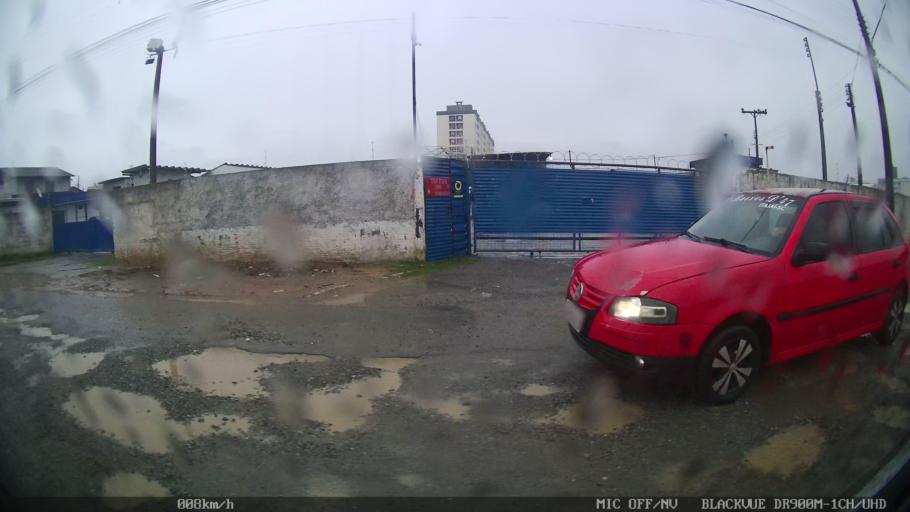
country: BR
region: Santa Catarina
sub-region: Itajai
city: Itajai
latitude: -26.9199
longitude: -48.6902
